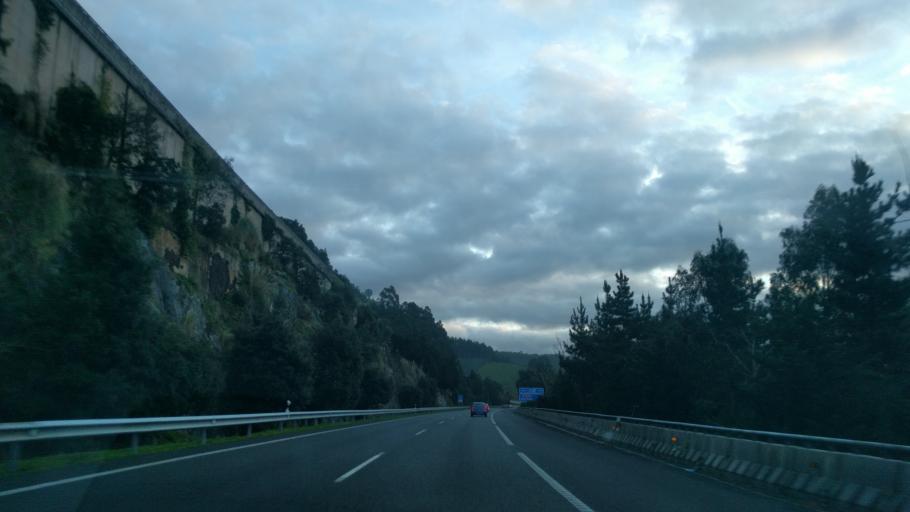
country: ES
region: Cantabria
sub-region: Provincia de Cantabria
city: Liendo
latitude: 43.3949
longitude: -3.3137
